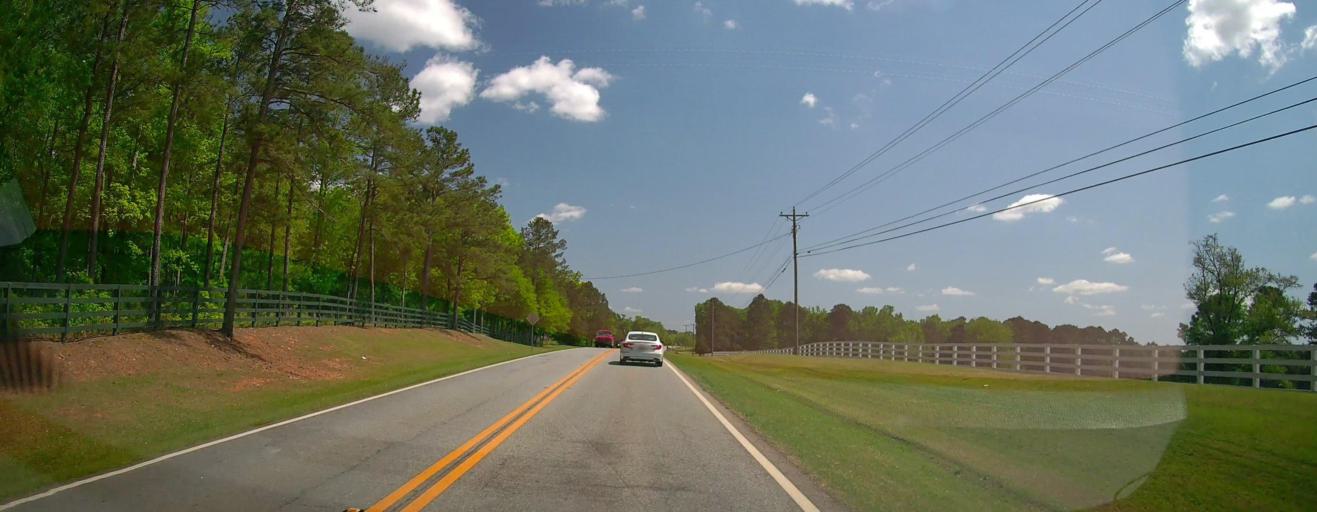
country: US
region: Georgia
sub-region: Putnam County
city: Eatonton
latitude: 33.2973
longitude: -83.3031
